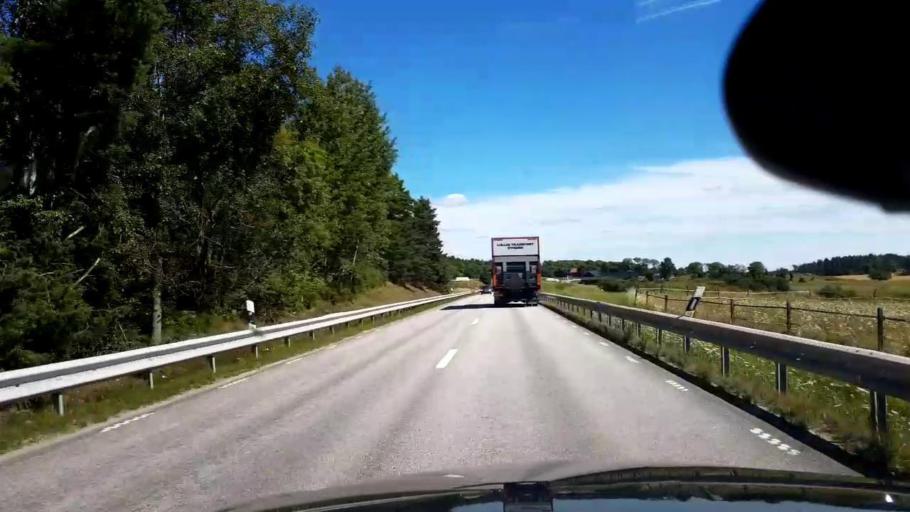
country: SE
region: Stockholm
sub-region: Sigtuna Kommun
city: Sigtuna
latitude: 59.6556
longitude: 17.6686
